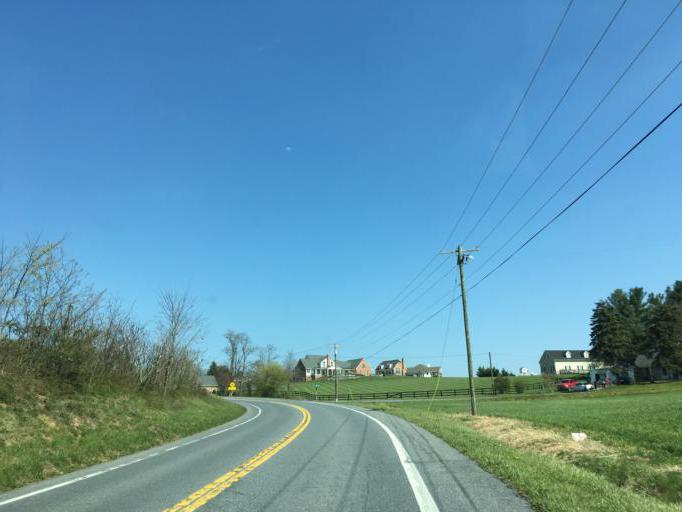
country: US
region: Maryland
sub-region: Carroll County
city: New Windsor
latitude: 39.4912
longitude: -77.1579
